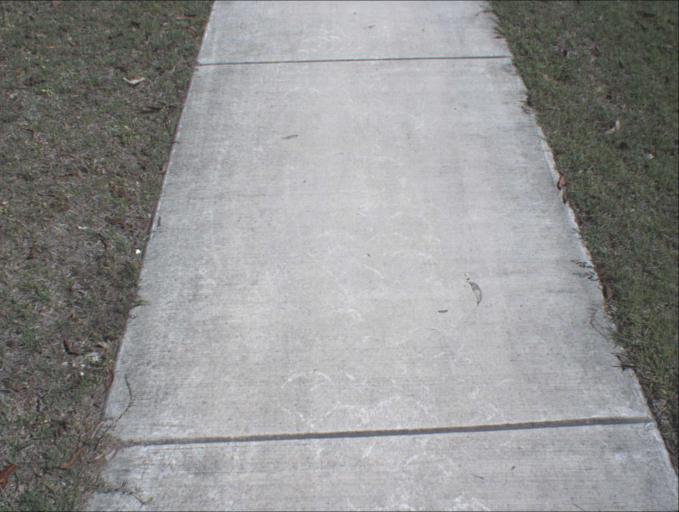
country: AU
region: Queensland
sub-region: Logan
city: Chambers Flat
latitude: -27.7466
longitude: 153.0539
